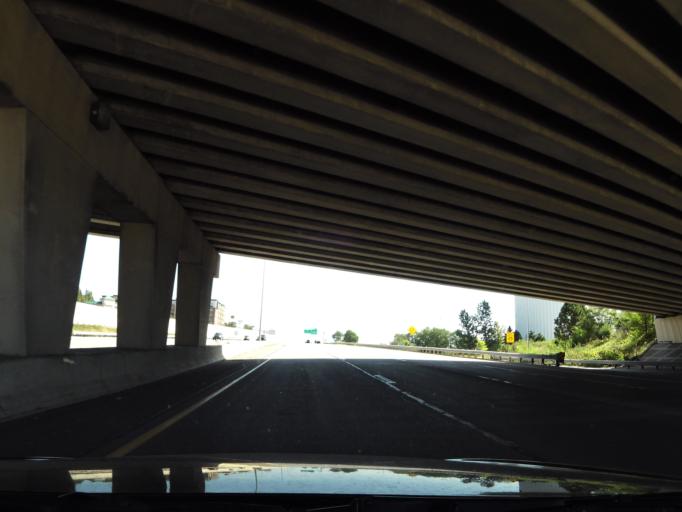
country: US
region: Minnesota
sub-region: Hennepin County
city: Minnetonka Mills
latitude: 44.9710
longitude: -93.4453
